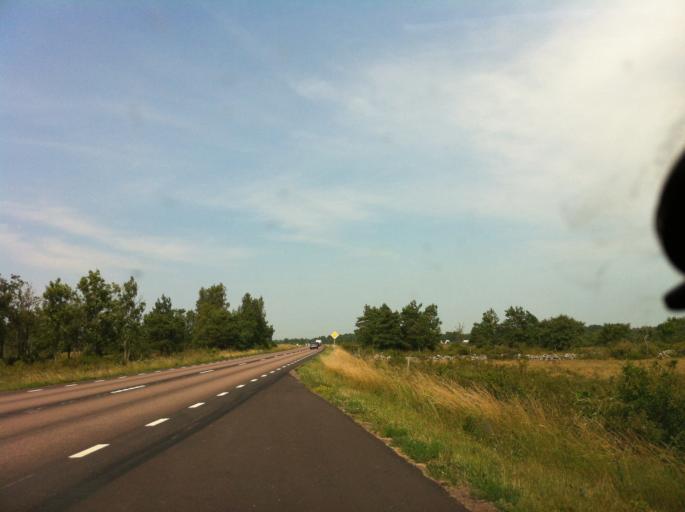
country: SE
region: Kalmar
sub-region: Borgholms Kommun
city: Borgholm
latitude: 57.0390
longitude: 16.8697
